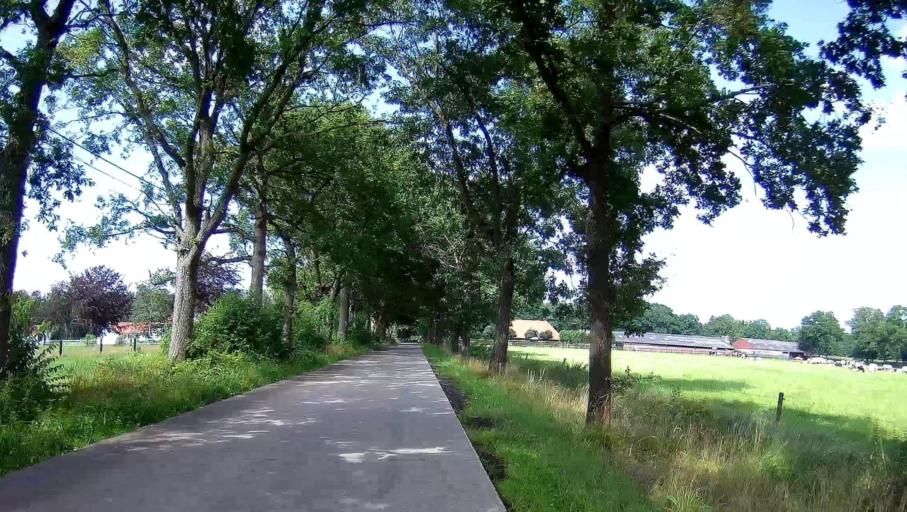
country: BE
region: Flanders
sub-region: Provincie Limburg
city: Leopoldsburg
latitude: 51.1698
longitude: 5.2609
